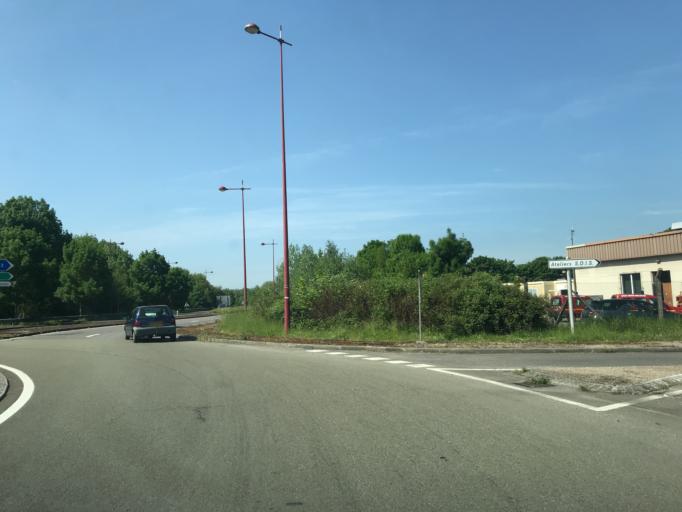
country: FR
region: Haute-Normandie
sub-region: Departement de la Seine-Maritime
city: Tourville-la-Riviere
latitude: 49.3354
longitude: 1.1139
